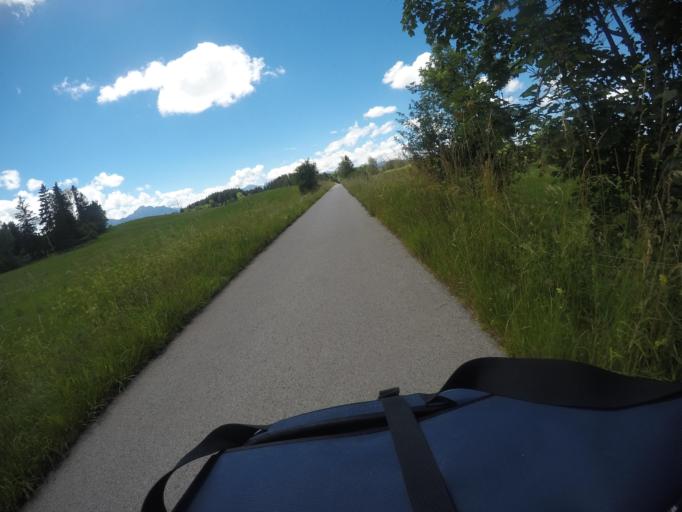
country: DE
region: Bavaria
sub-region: Swabia
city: Lechbruck
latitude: 47.6836
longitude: 10.7577
